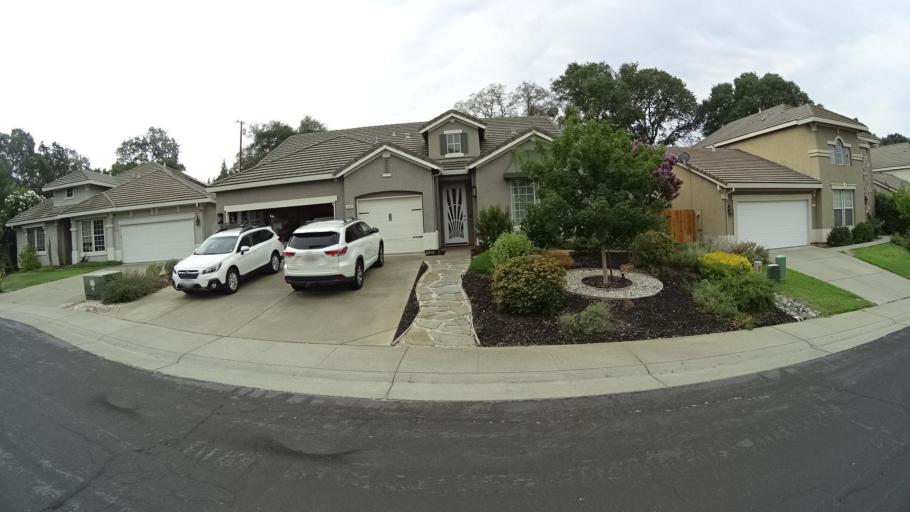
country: US
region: California
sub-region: Placer County
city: Rocklin
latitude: 38.7828
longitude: -121.2021
